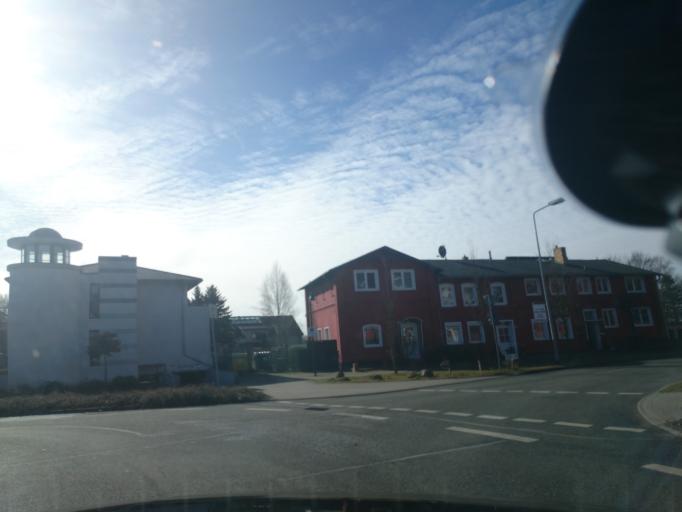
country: DE
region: Mecklenburg-Vorpommern
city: Elmenhorst
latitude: 54.1690
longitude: 12.0366
